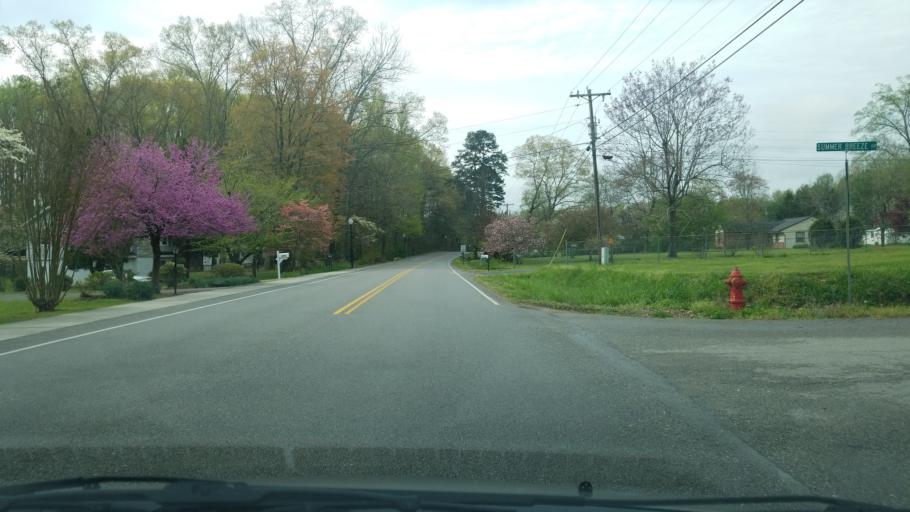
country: US
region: Tennessee
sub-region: Hamilton County
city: Collegedale
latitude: 35.0365
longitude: -85.0570
